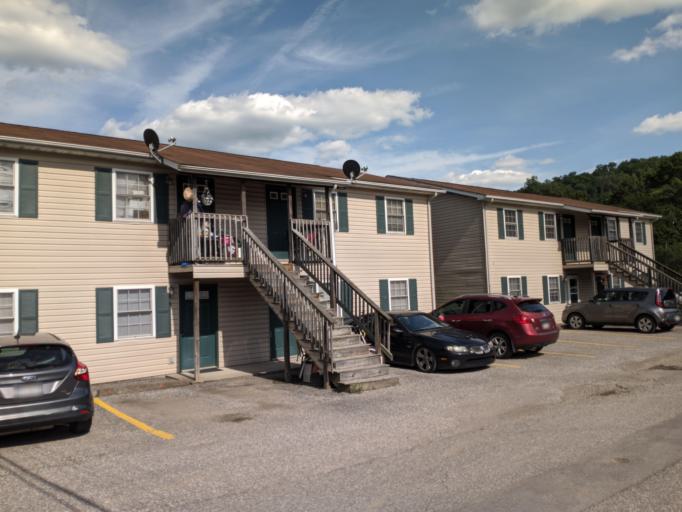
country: US
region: West Virginia
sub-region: Ohio County
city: Bethlehem
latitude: 40.0481
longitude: -80.6374
